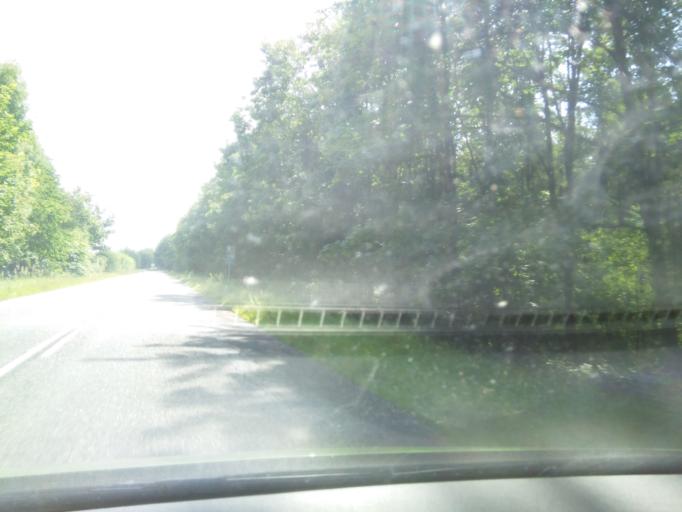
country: DK
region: Central Jutland
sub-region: Arhus Kommune
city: Solbjerg
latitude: 55.9682
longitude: 10.0772
